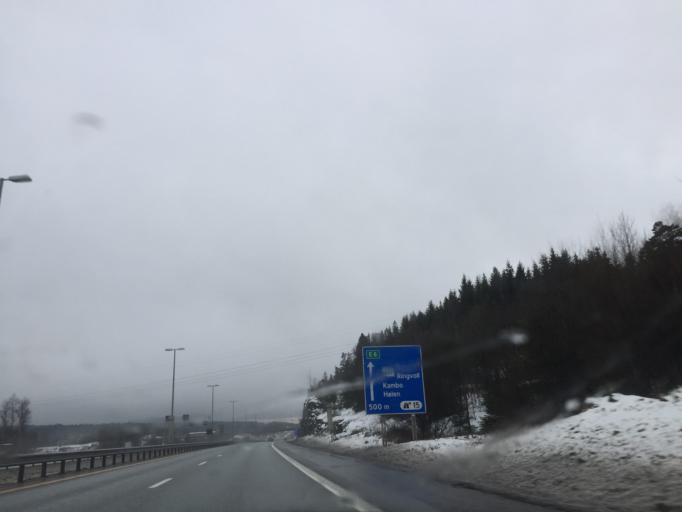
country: NO
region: Akershus
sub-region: Vestby
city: Vestby
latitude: 59.5221
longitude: 10.7282
